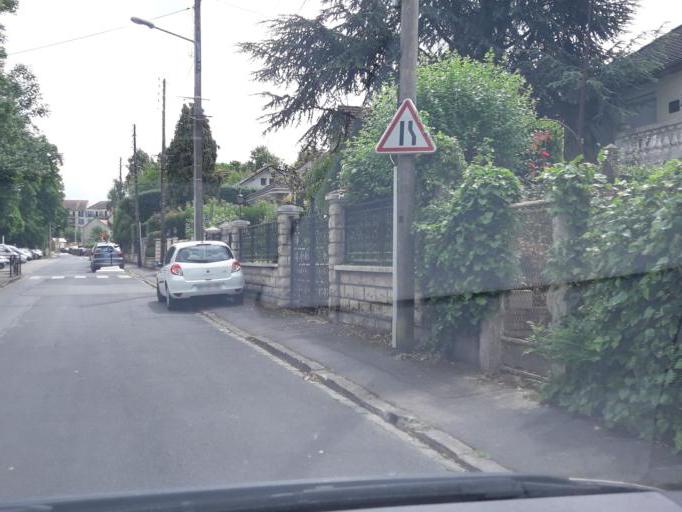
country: FR
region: Ile-de-France
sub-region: Departement de l'Essonne
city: Villemoisson-sur-Orge
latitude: 48.6638
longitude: 2.3444
